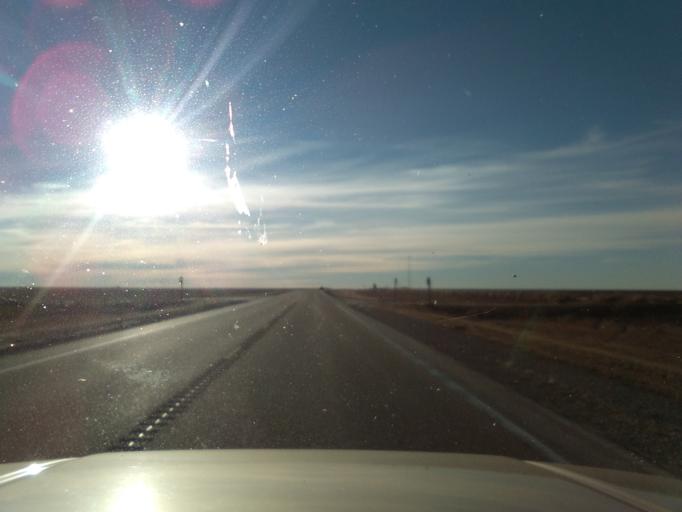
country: US
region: Kansas
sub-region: Sheridan County
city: Hoxie
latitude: 39.4862
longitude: -100.7014
